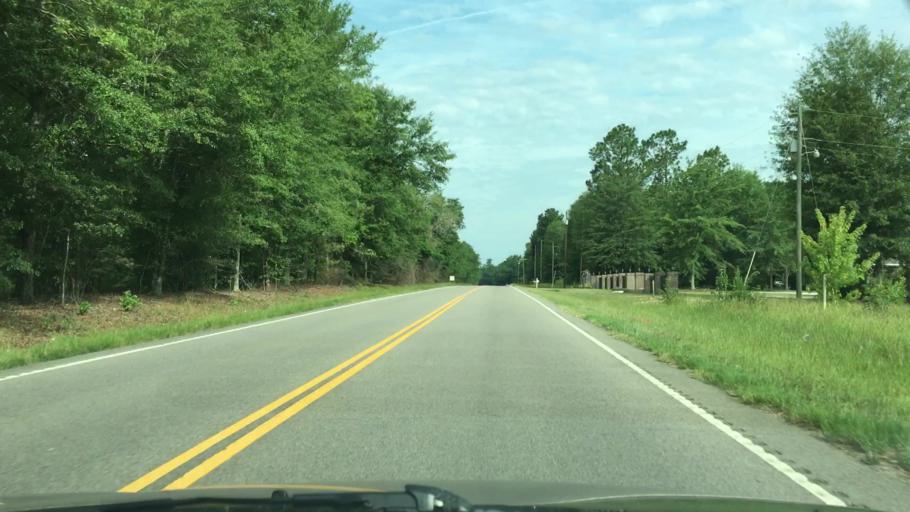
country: US
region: South Carolina
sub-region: Barnwell County
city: Williston
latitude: 33.6633
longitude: -81.3928
